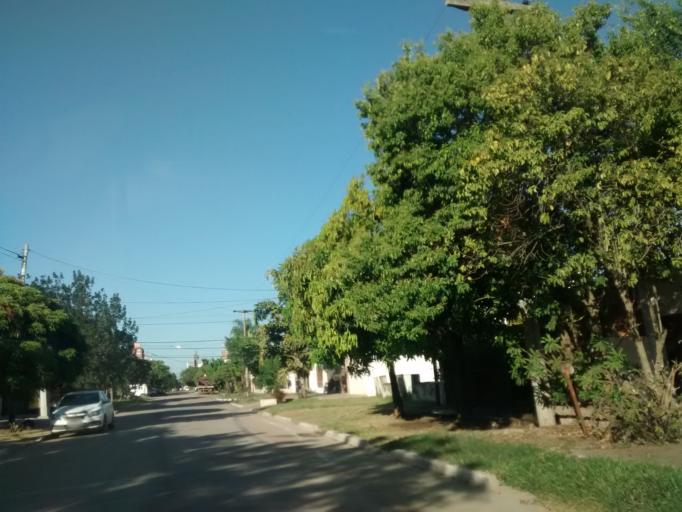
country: AR
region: Chaco
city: Resistencia
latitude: -27.4608
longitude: -59.0007
